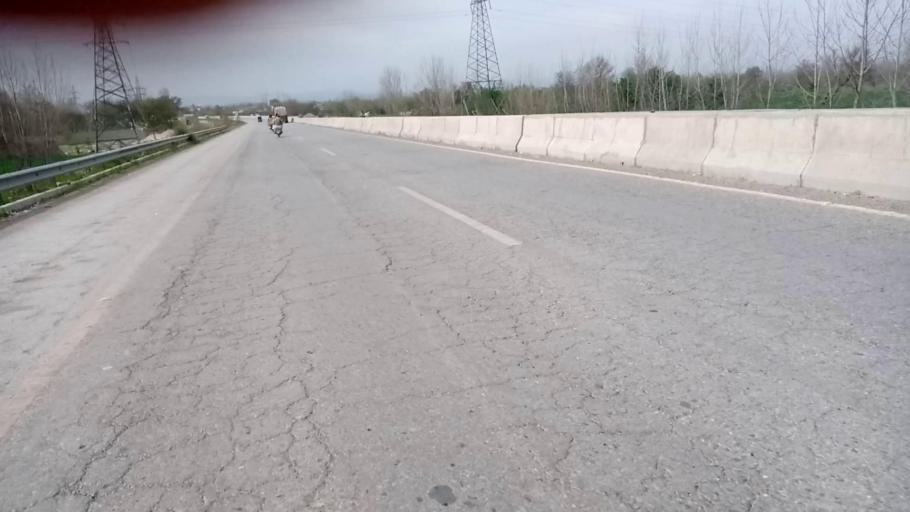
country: PK
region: Khyber Pakhtunkhwa
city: Peshawar
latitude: 34.0632
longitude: 71.6033
